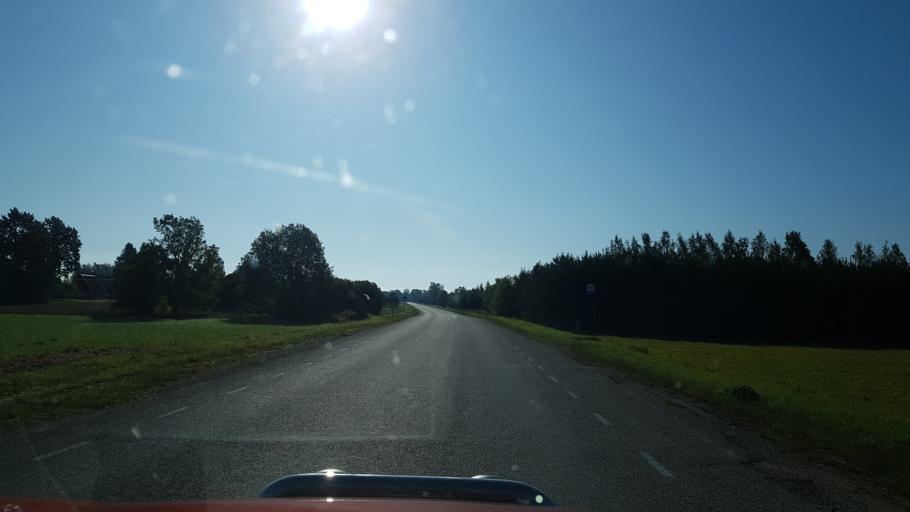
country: EE
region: Jogevamaa
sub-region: Tabivere vald
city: Tabivere
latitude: 58.6759
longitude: 26.6724
